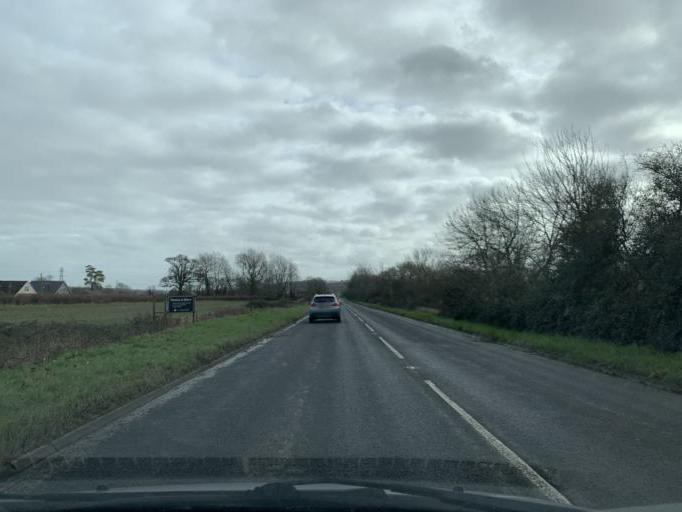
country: GB
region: England
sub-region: Wiltshire
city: Wilton
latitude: 51.0658
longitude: -1.8440
